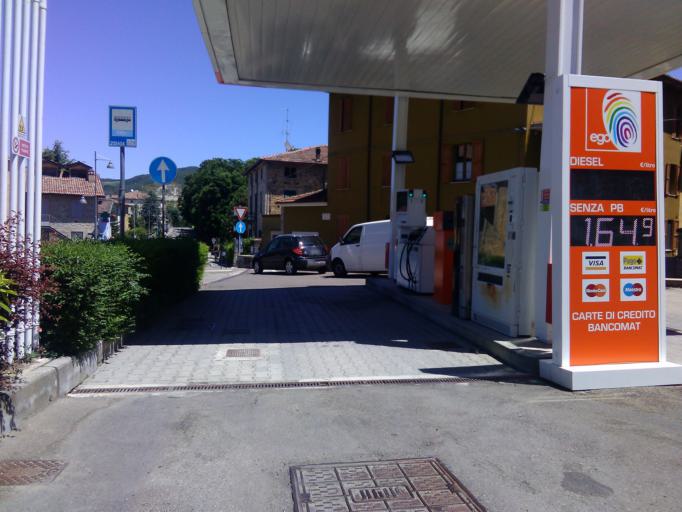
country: IT
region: Emilia-Romagna
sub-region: Provincia di Parma
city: Calestano
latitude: 44.6011
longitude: 10.1221
